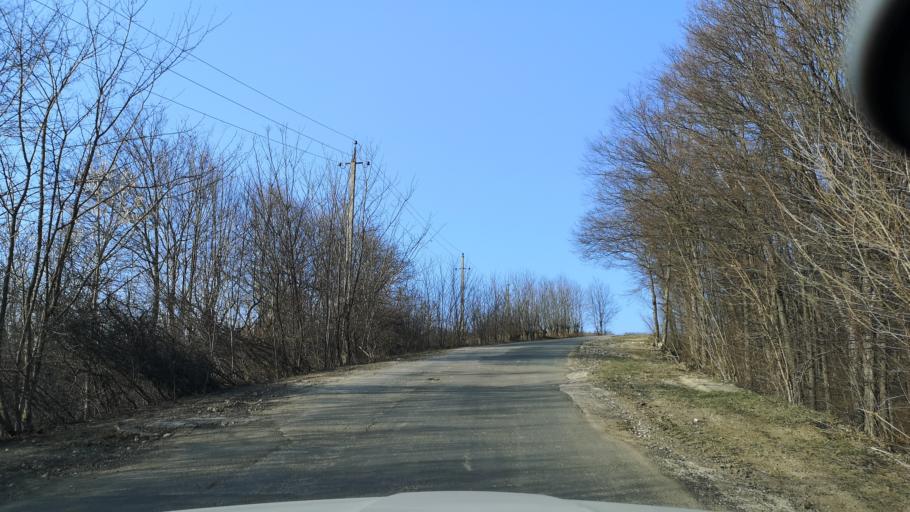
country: MD
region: Nisporeni
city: Nisporeni
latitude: 47.0898
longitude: 28.3164
